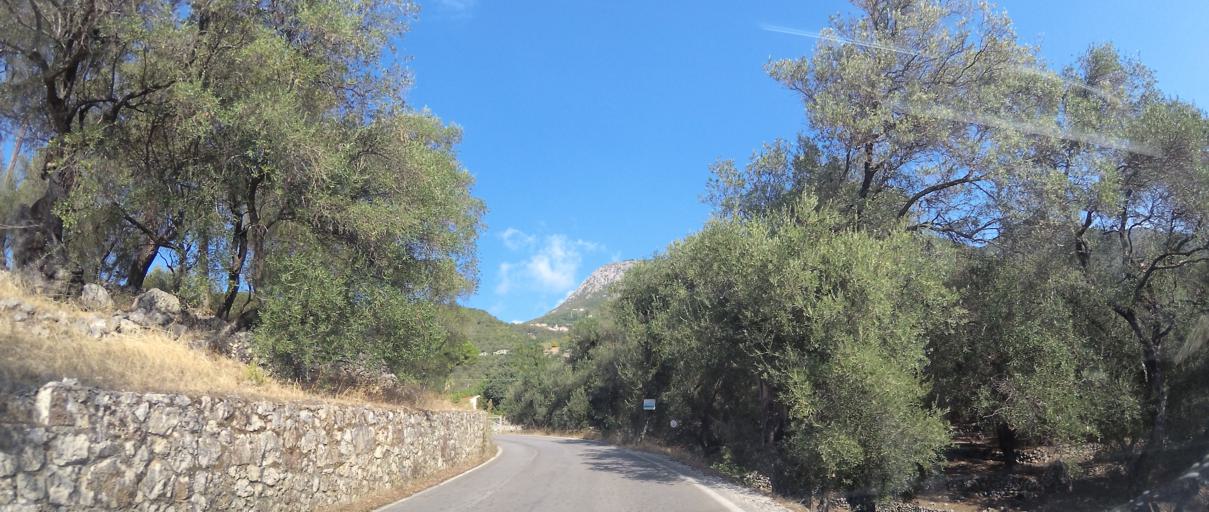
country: GR
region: Ionian Islands
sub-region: Nomos Kerkyras
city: Kontokali
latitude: 39.7135
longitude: 19.8471
